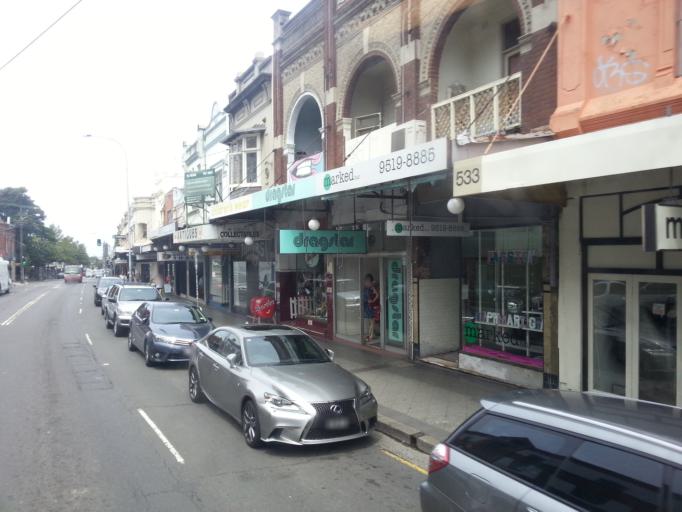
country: AU
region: New South Wales
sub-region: Marrickville
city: Newtown
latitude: -33.9035
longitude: 151.1799
